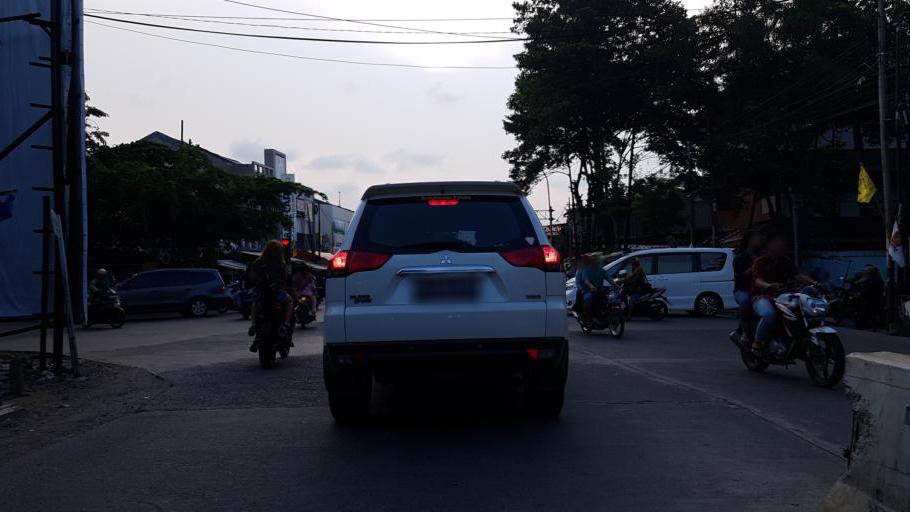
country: ID
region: Jakarta Raya
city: Jakarta
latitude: -6.1385
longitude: 106.7780
